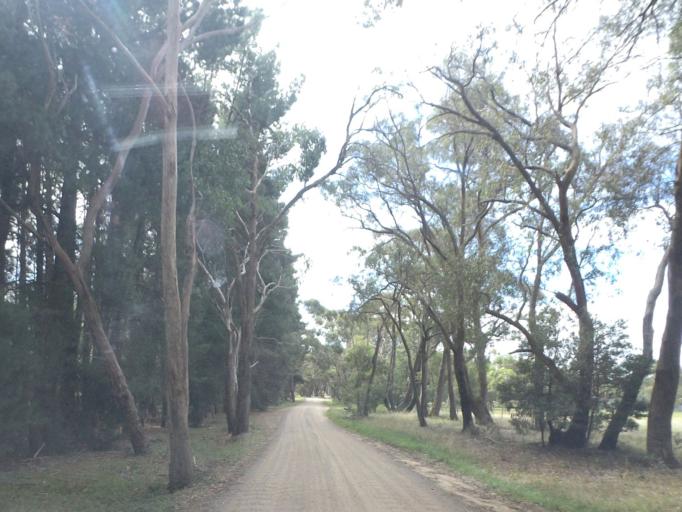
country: AU
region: Victoria
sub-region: Hume
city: Sunbury
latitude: -37.3677
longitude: 144.5521
